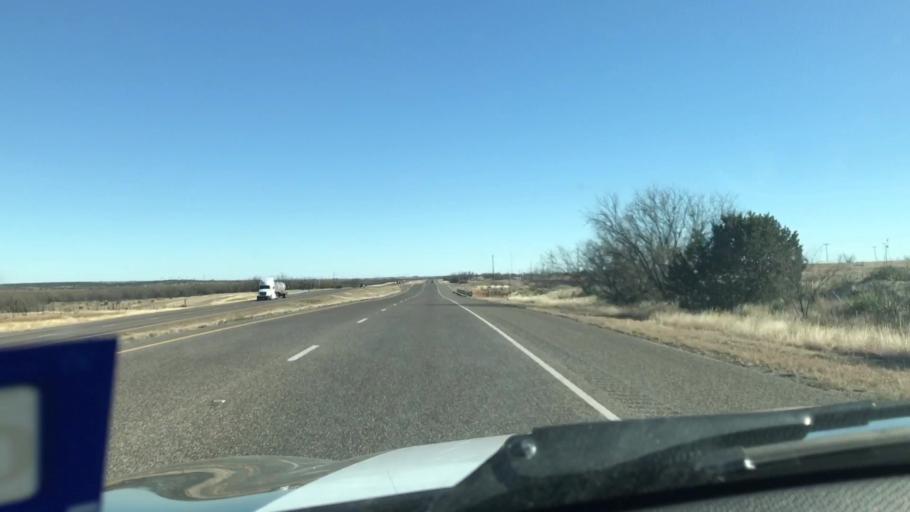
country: US
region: Texas
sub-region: Scurry County
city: Snyder
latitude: 32.8393
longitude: -100.9959
